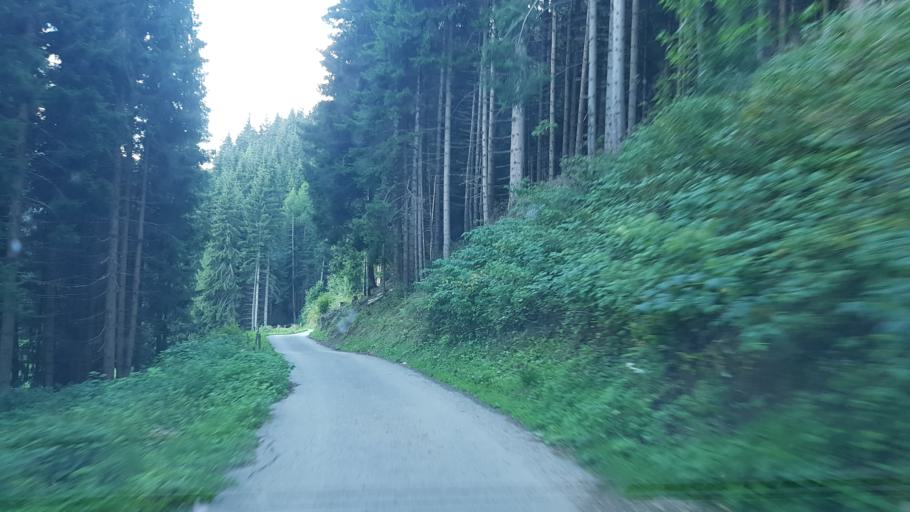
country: IT
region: Veneto
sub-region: Provincia di Belluno
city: San Pietro di Cadore
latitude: 46.5899
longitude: 12.5913
